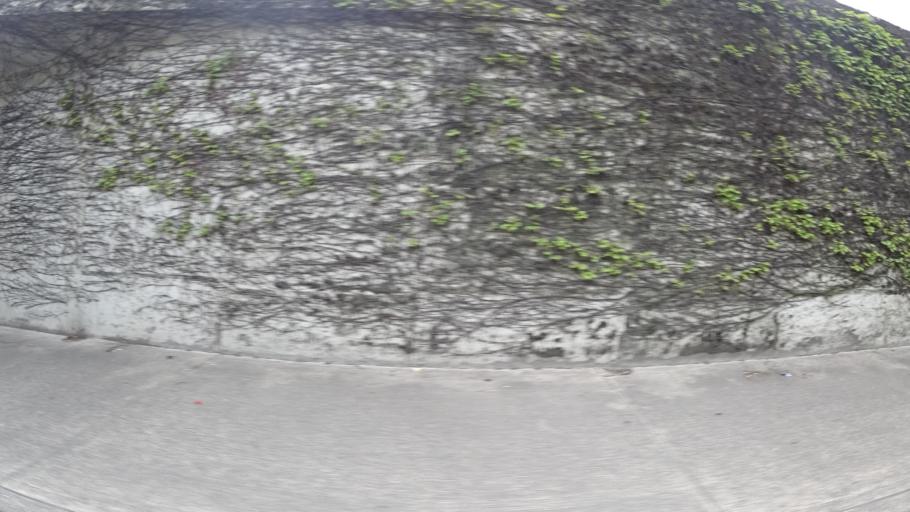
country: US
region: Oregon
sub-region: Multnomah County
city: Portland
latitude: 45.5151
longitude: -122.6876
